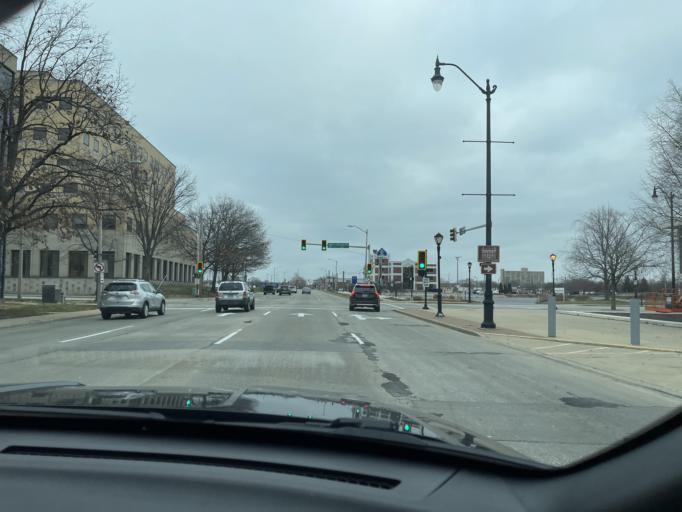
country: US
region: Illinois
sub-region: Sangamon County
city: Springfield
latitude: 39.8039
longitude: -89.6469
